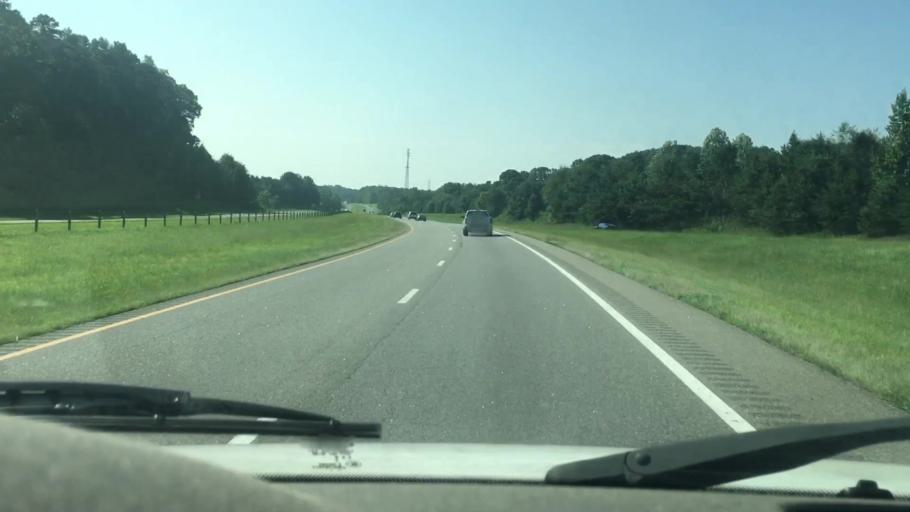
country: US
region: North Carolina
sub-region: Lincoln County
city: Lowesville
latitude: 35.3812
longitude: -81.0007
